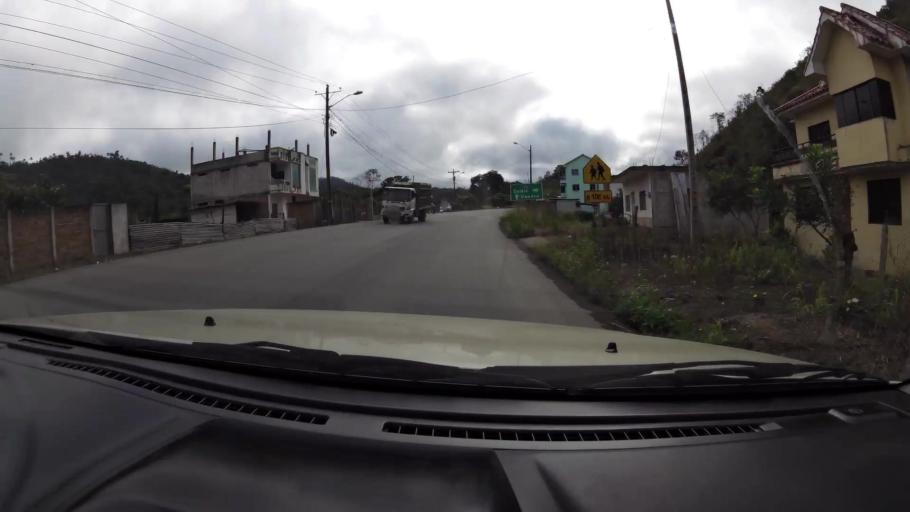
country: EC
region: El Oro
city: Pasaje
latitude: -3.3202
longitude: -79.6789
